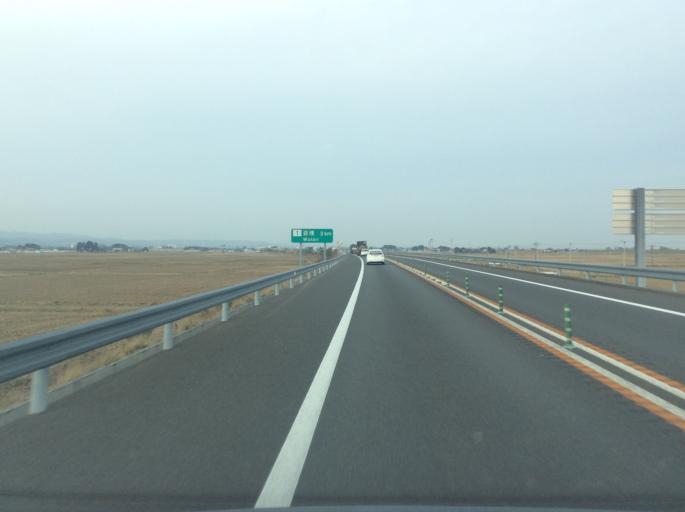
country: JP
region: Miyagi
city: Iwanuma
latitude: 38.0672
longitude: 140.8929
